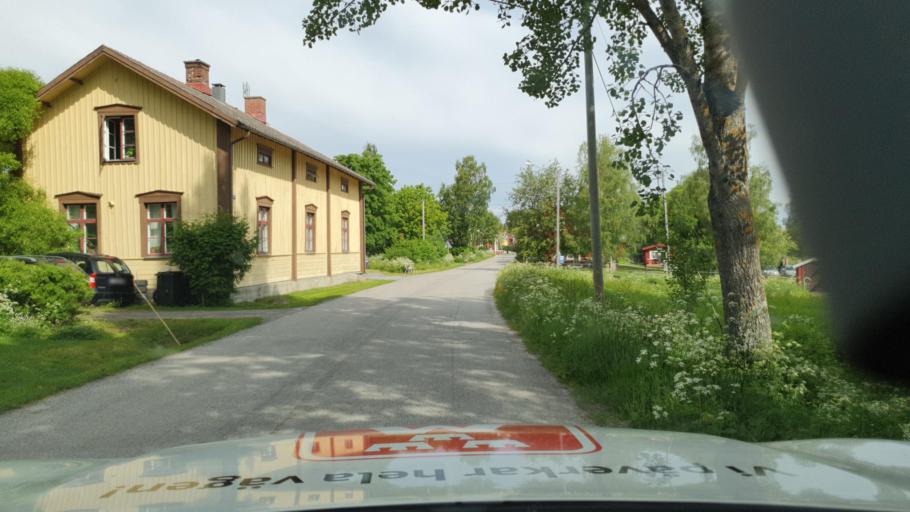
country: SE
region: Vaesterbotten
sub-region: Robertsfors Kommun
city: Robertsfors
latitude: 63.9909
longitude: 20.8895
